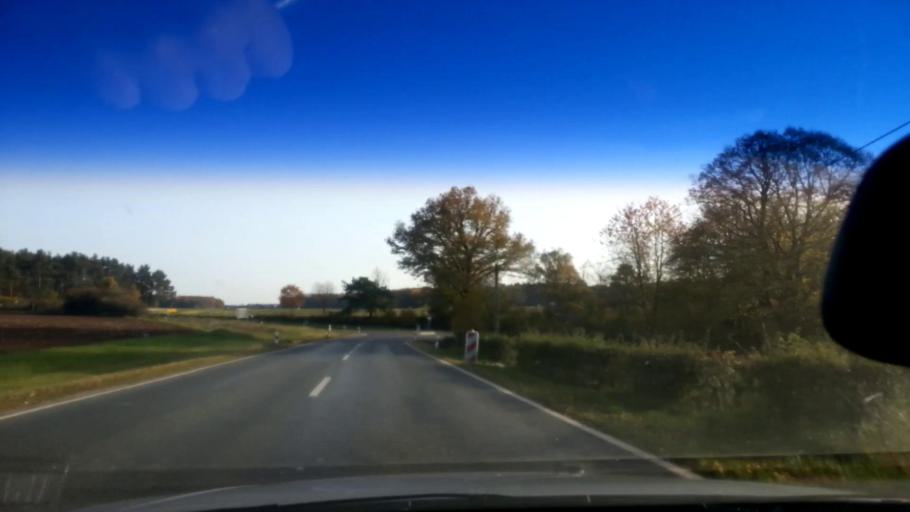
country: DE
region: Bavaria
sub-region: Upper Franconia
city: Poxdorf
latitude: 49.9760
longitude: 11.1113
